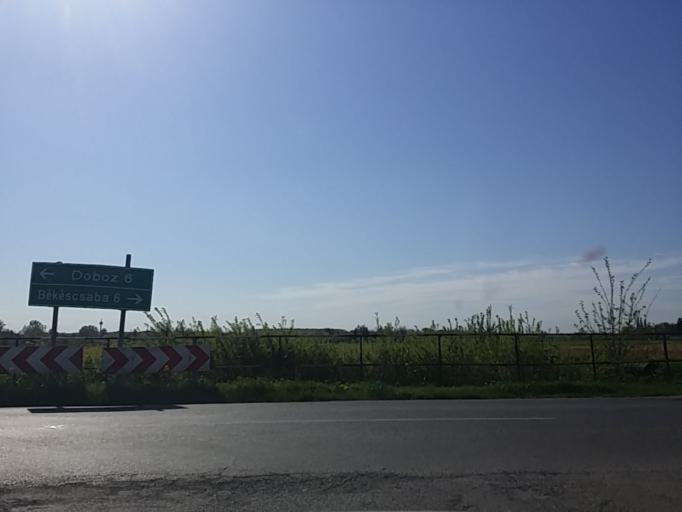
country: HU
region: Bekes
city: Bekes
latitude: 46.7080
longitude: 21.1734
